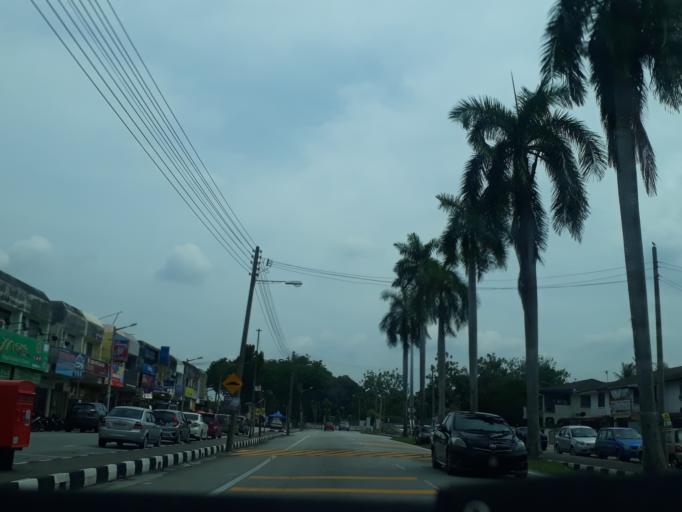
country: MY
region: Perak
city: Ipoh
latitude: 4.5948
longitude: 101.1256
